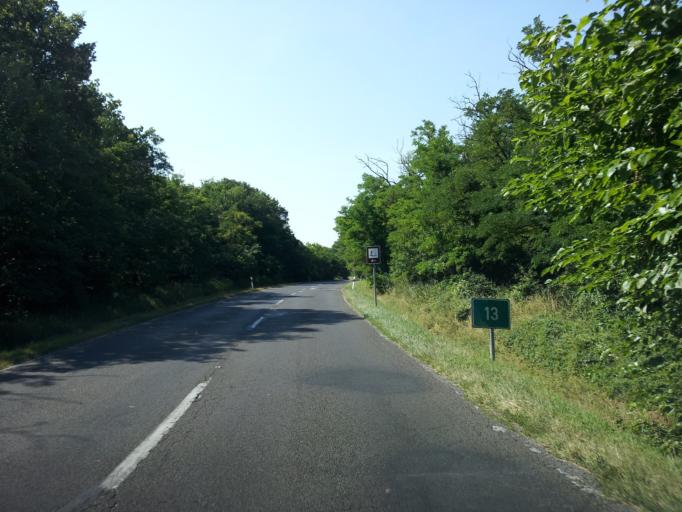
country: HU
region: Fejer
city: Lovasbereny
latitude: 47.2717
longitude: 18.5270
